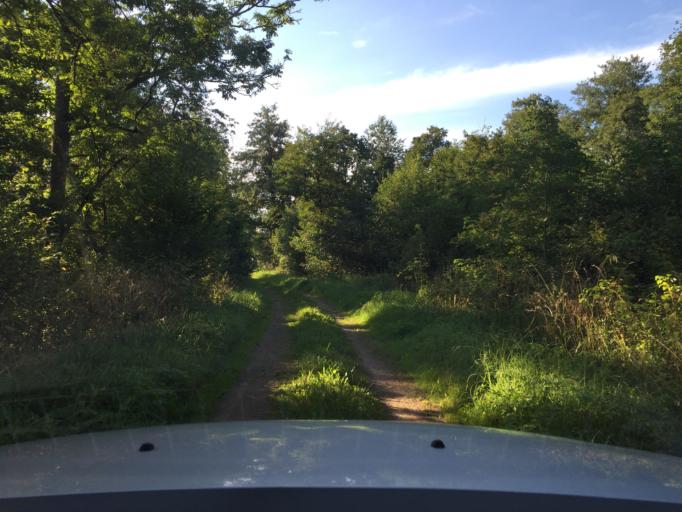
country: SE
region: Skane
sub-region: Hassleholms Kommun
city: Sosdala
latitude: 56.0267
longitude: 13.7021
